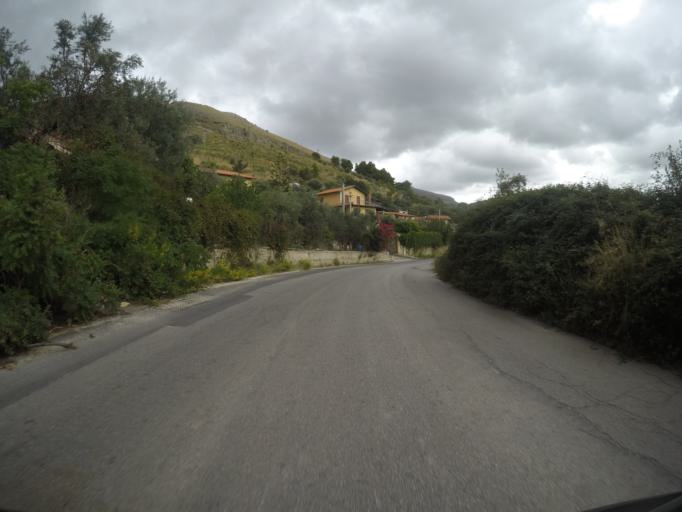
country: IT
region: Sicily
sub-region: Palermo
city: Montelepre
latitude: 38.0953
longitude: 13.1710
